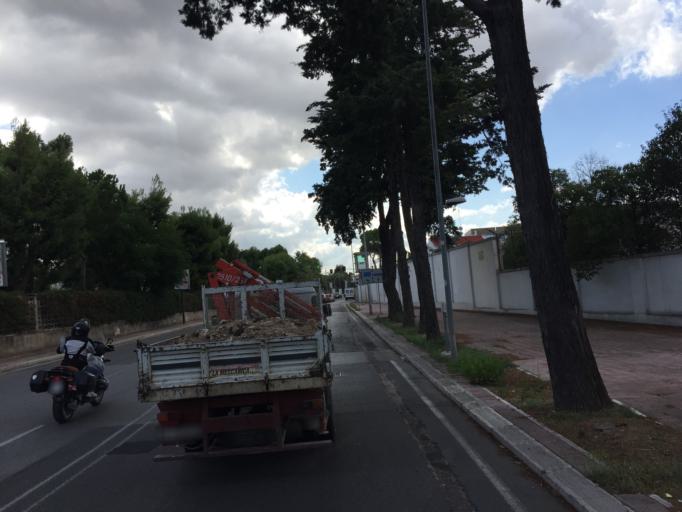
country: IT
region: Apulia
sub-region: Provincia di Bari
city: Bari
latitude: 41.0950
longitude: 16.8830
